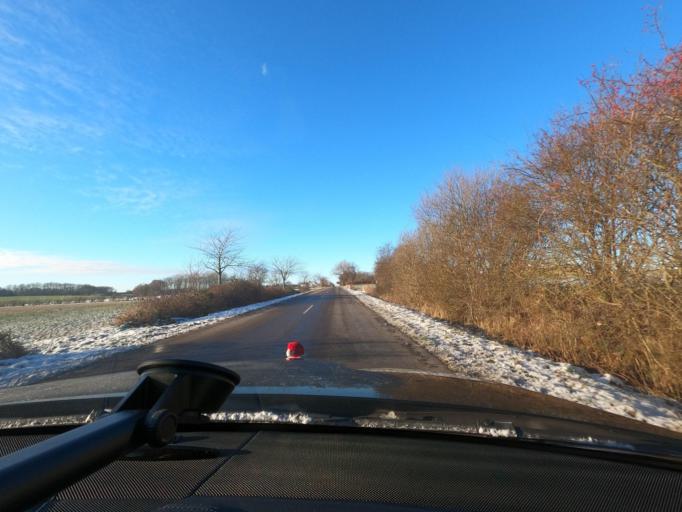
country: DK
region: South Denmark
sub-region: Sonderborg Kommune
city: Horuphav
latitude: 54.8717
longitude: 9.9405
